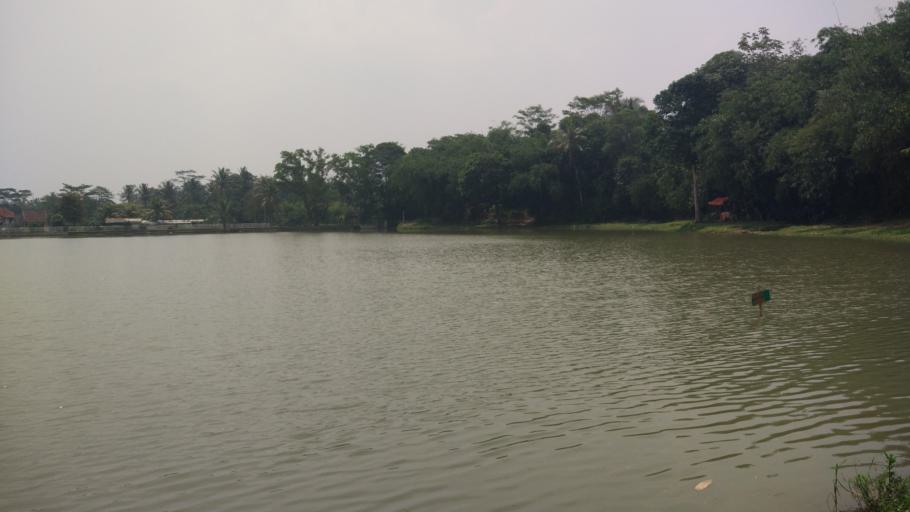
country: ID
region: West Java
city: Ciampea
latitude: -6.5757
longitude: 106.7303
